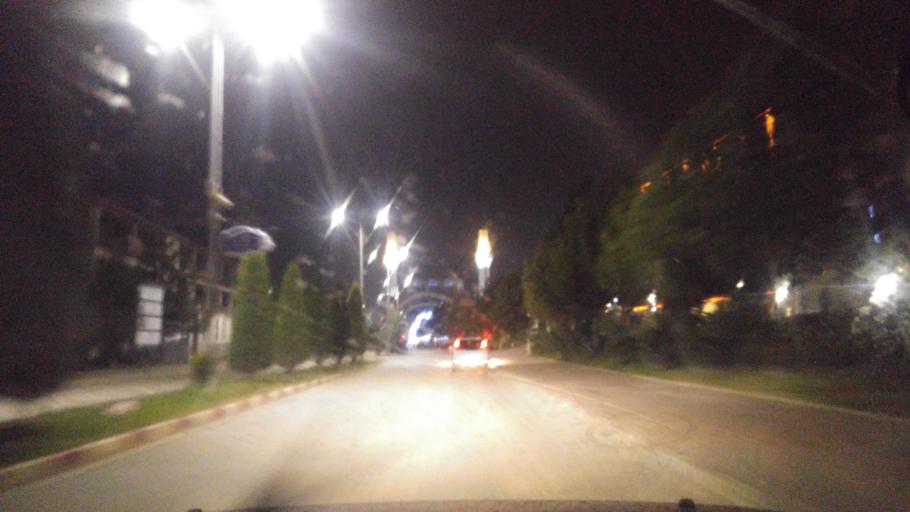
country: TR
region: Karabuk
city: Karabuk
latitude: 41.2102
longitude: 32.6559
